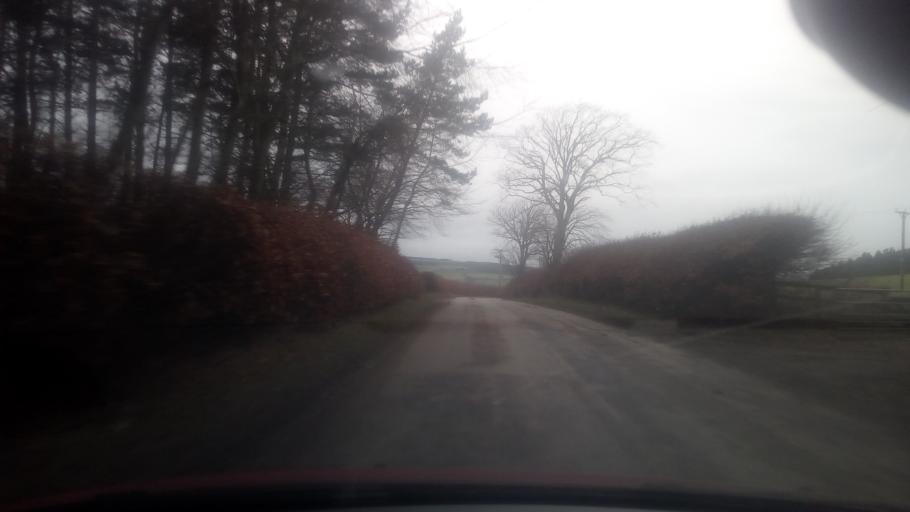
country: GB
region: Scotland
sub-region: The Scottish Borders
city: Jedburgh
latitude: 55.4756
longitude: -2.5170
